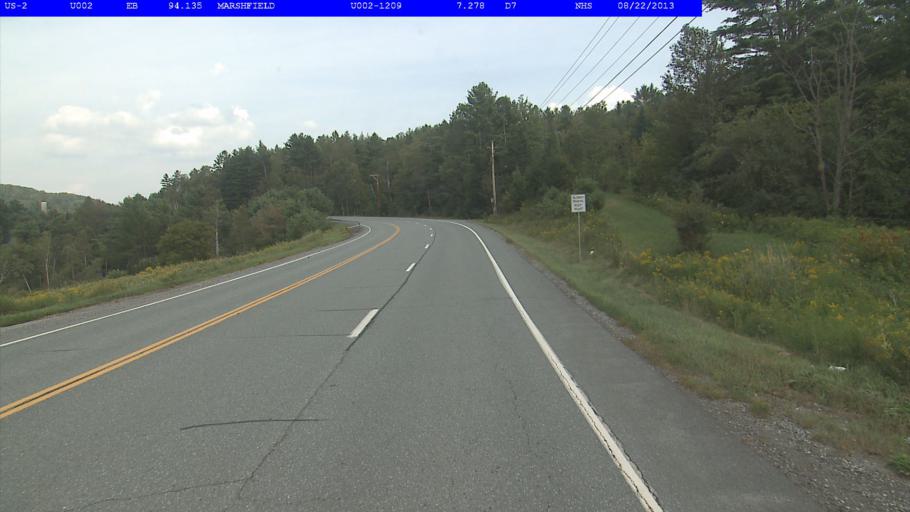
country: US
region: Vermont
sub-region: Caledonia County
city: Hardwick
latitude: 44.3549
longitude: -72.3394
